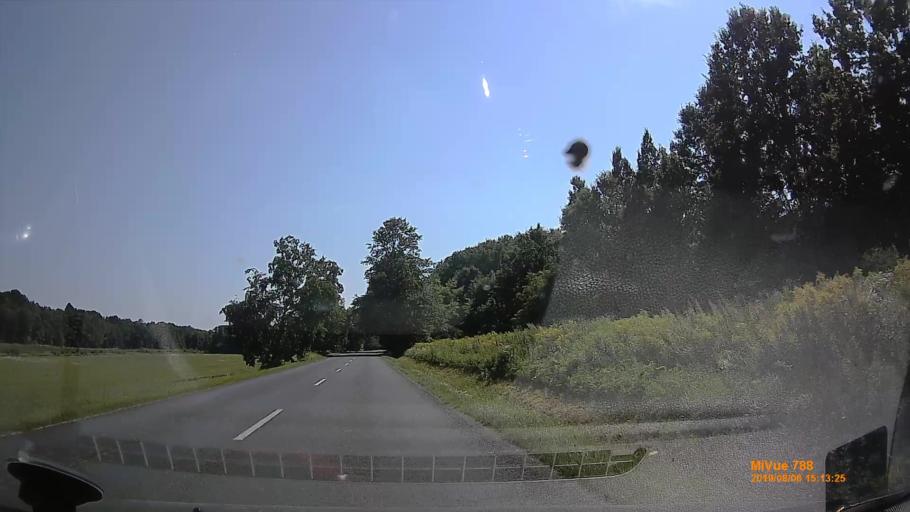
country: HU
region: Zala
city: Murakeresztur
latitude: 46.3545
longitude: 16.9779
